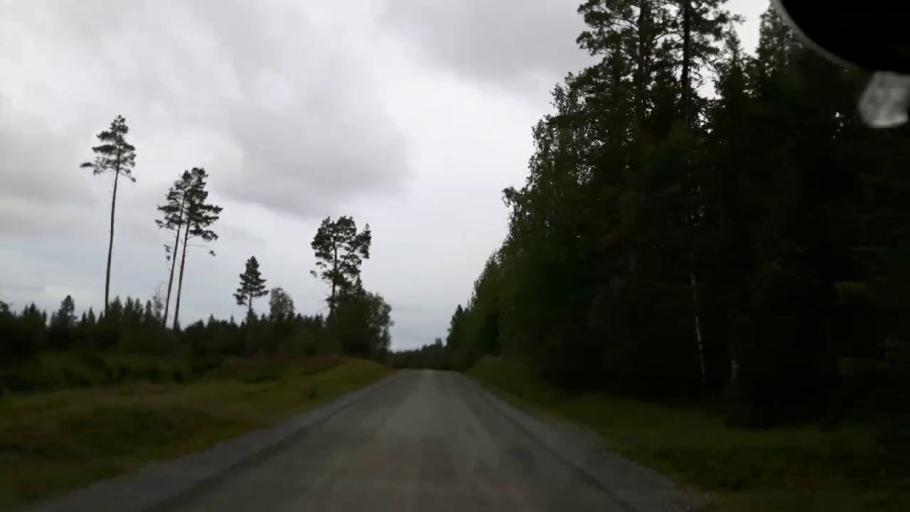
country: SE
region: Jaemtland
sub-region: OEstersunds Kommun
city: Ostersund
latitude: 63.1031
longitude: 14.5463
